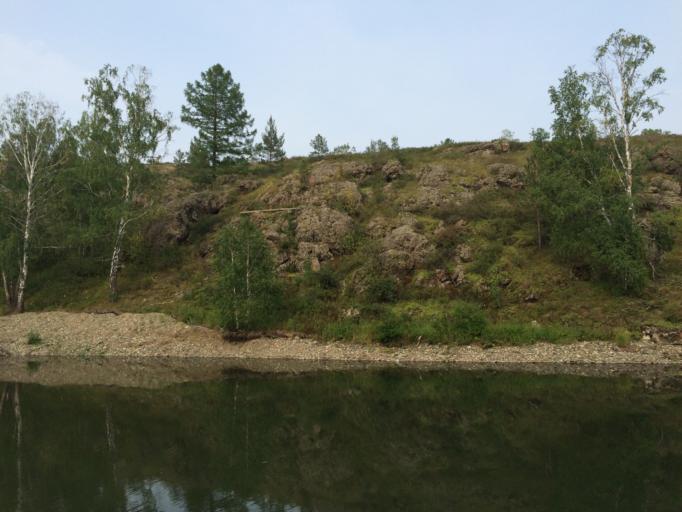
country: RU
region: Bashkortostan
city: Abzakovo
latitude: 53.7959
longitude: 58.6303
